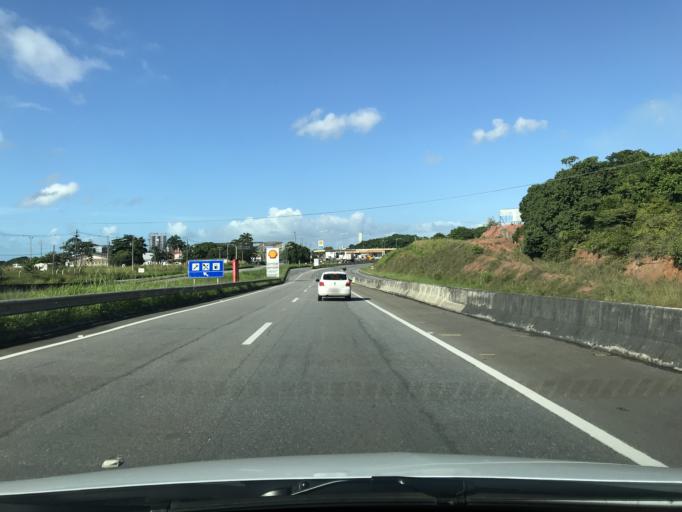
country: BR
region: Pernambuco
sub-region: Ipojuca
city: Ipojuca
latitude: -8.3643
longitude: -35.0077
